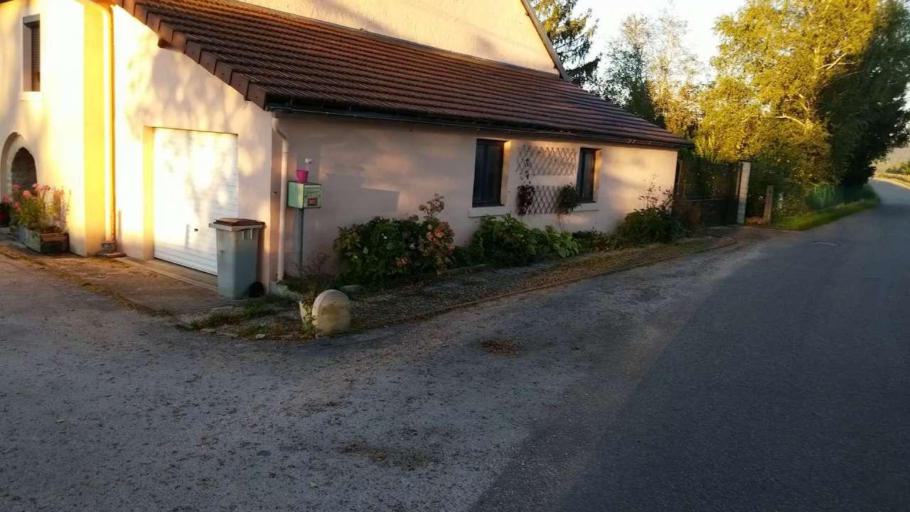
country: FR
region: Franche-Comte
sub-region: Departement du Jura
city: Perrigny
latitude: 46.7325
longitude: 5.5721
